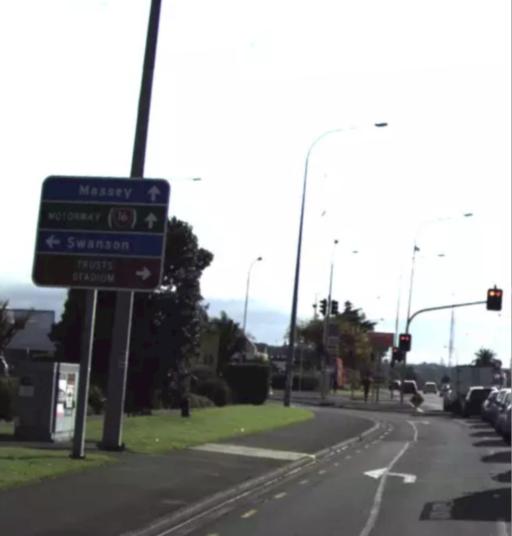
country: NZ
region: Auckland
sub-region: Auckland
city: Rosebank
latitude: -36.8576
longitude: 174.6298
